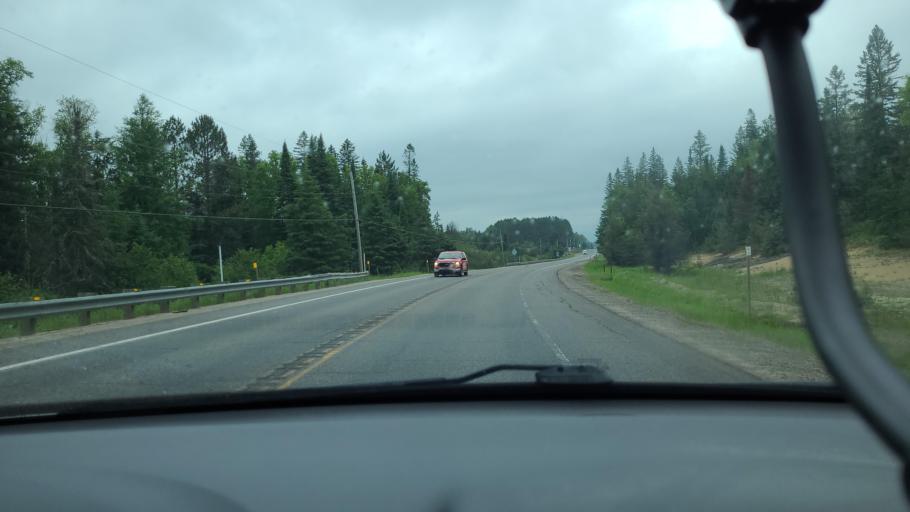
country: CA
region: Quebec
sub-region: Laurentides
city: Riviere-Rouge
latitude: 46.3713
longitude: -74.8481
